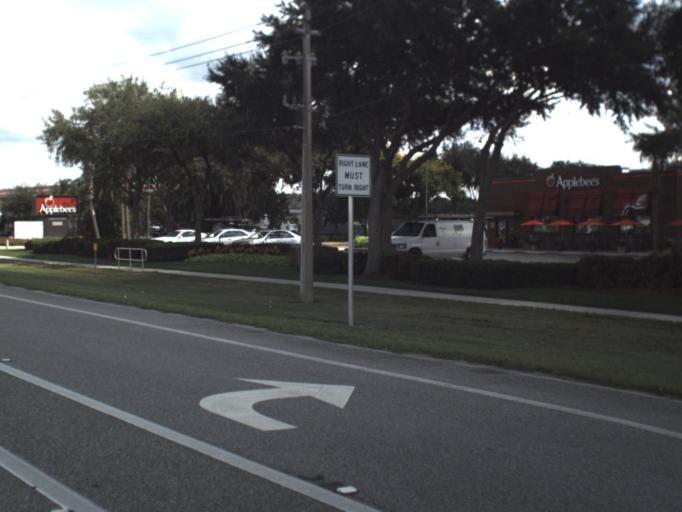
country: US
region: Florida
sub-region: Sarasota County
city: Fruitville
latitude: 27.3379
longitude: -82.4583
